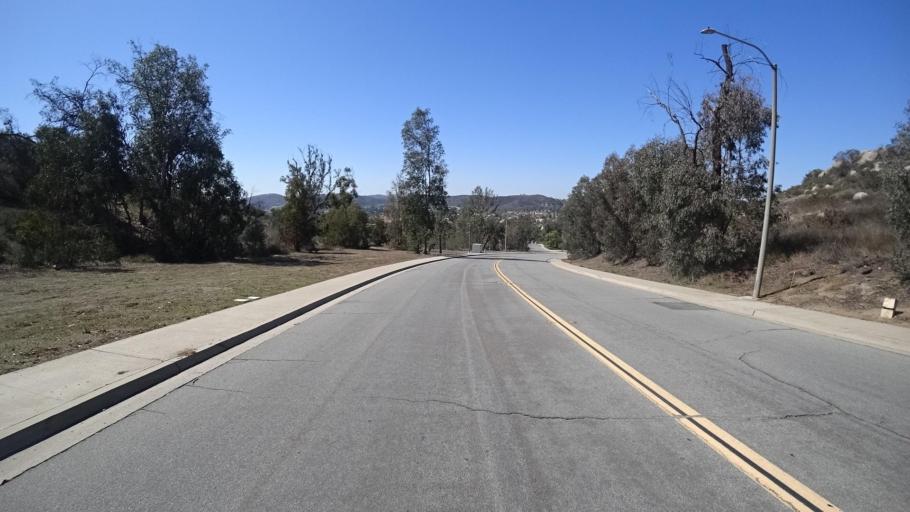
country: US
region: California
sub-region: San Diego County
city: Rancho San Diego
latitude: 32.7508
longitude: -116.9219
